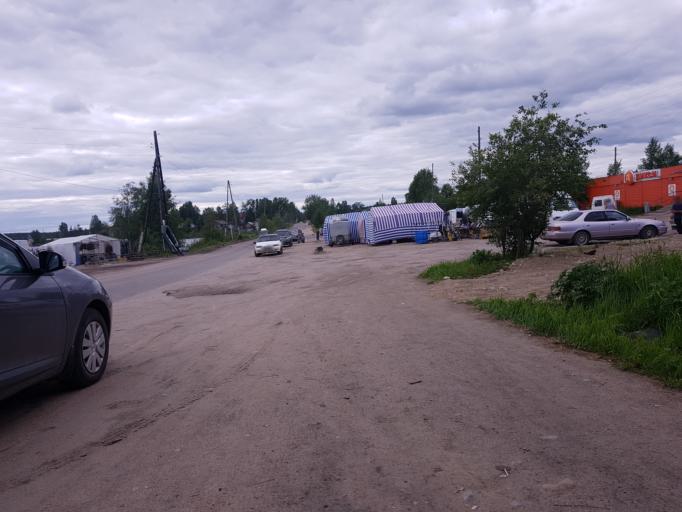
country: RU
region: Republic of Karelia
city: Kalevala
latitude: 65.1980
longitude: 31.1803
